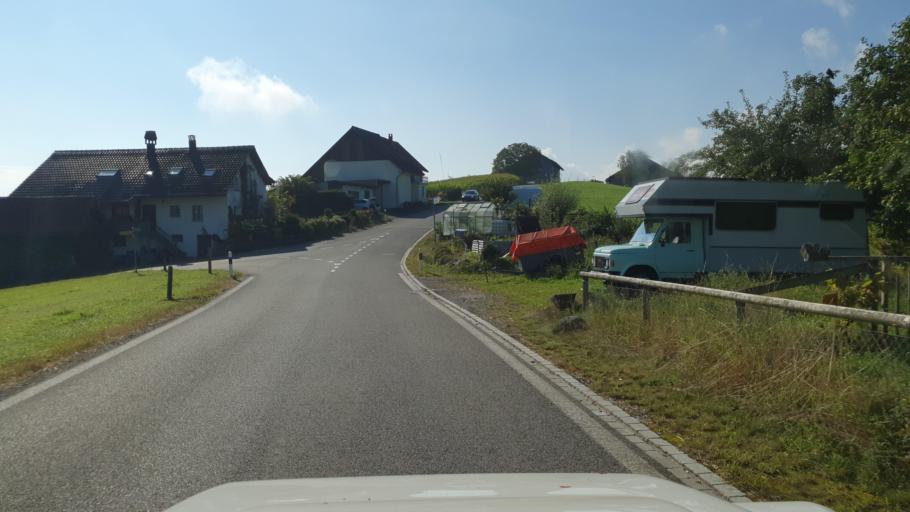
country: CH
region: Aargau
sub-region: Bezirk Muri
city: Waltenschwil
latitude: 47.3172
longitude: 8.2912
